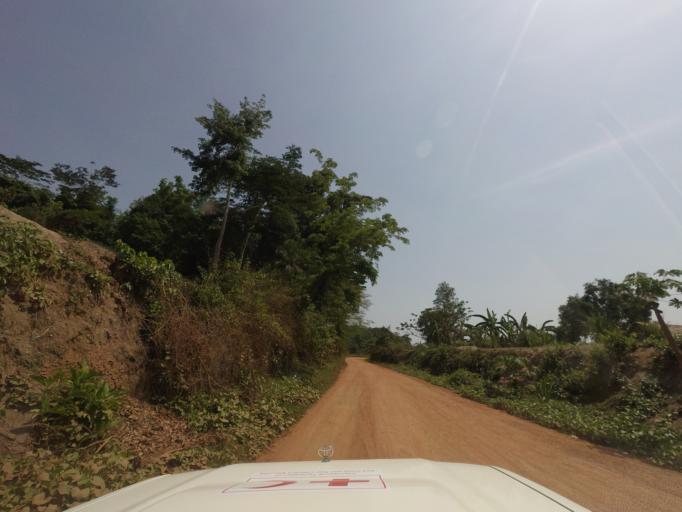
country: GN
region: Nzerekore
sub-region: Yomou
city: Yomou
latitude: 7.3411
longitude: -9.4998
